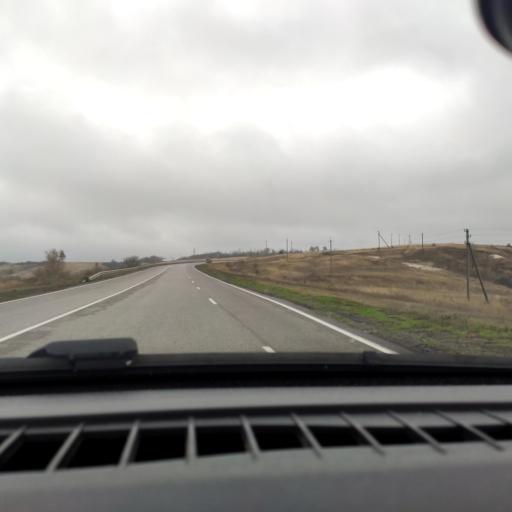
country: RU
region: Voronezj
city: Uryv-Pokrovka
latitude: 51.1334
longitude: 39.0464
